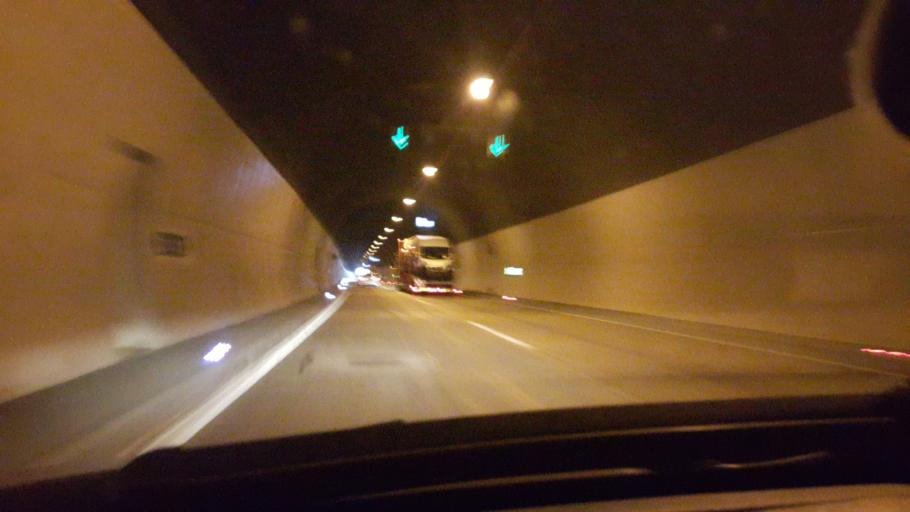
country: SI
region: Slovenska Konjice
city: Slovenske Konjice
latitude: 46.3132
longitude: 15.4577
